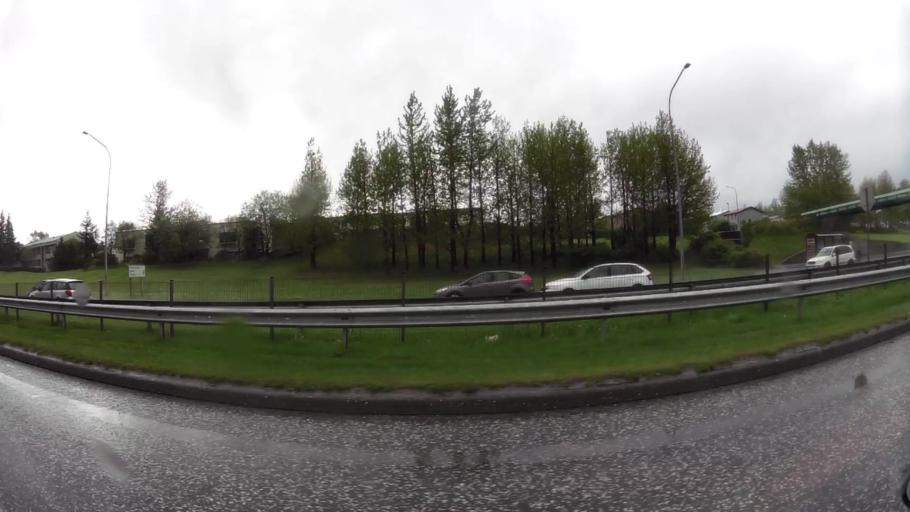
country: IS
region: Capital Region
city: Reykjavik
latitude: 64.1287
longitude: -21.8698
